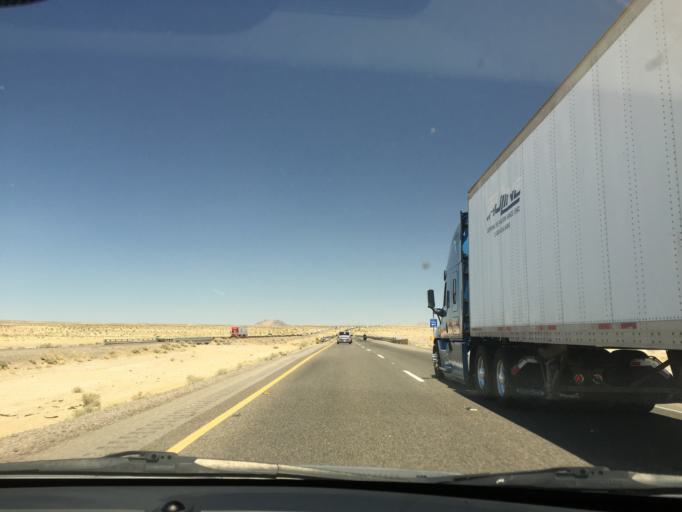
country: US
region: California
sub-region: San Bernardino County
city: Fort Irwin
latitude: 34.9960
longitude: -116.5703
